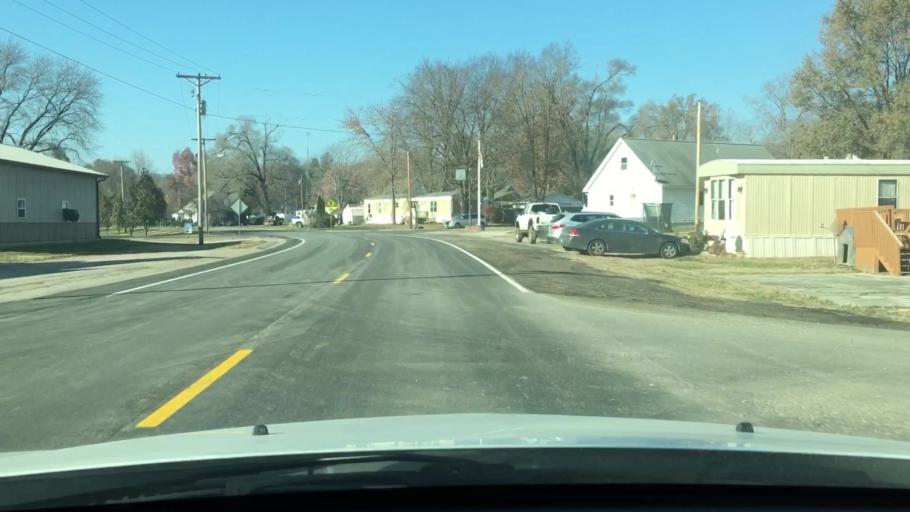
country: US
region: Illinois
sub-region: Fulton County
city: Astoria
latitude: 40.1288
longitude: -90.3720
